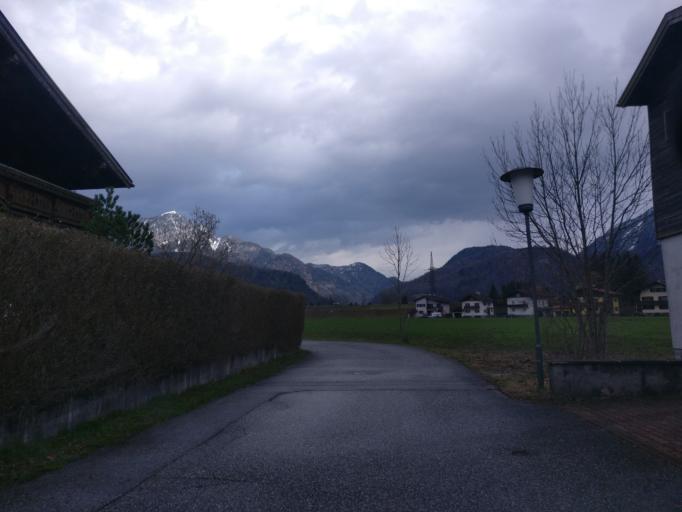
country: AT
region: Salzburg
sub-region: Politischer Bezirk Hallein
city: Golling an der Salzach
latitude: 47.5897
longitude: 13.1650
